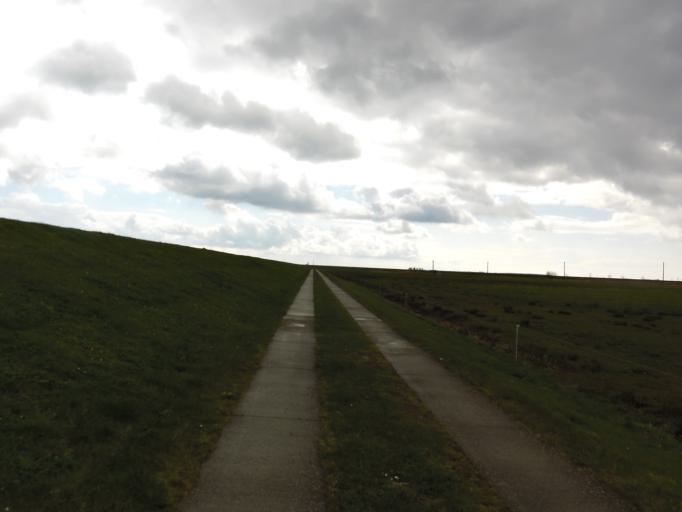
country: DE
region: Mecklenburg-Vorpommern
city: Barth
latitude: 54.4183
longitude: 12.7968
